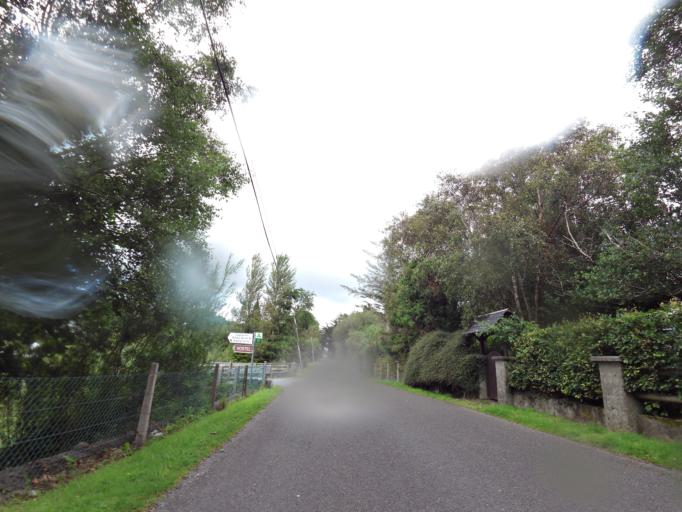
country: IE
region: Connaught
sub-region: County Galway
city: Oughterard
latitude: 53.4210
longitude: -9.3292
